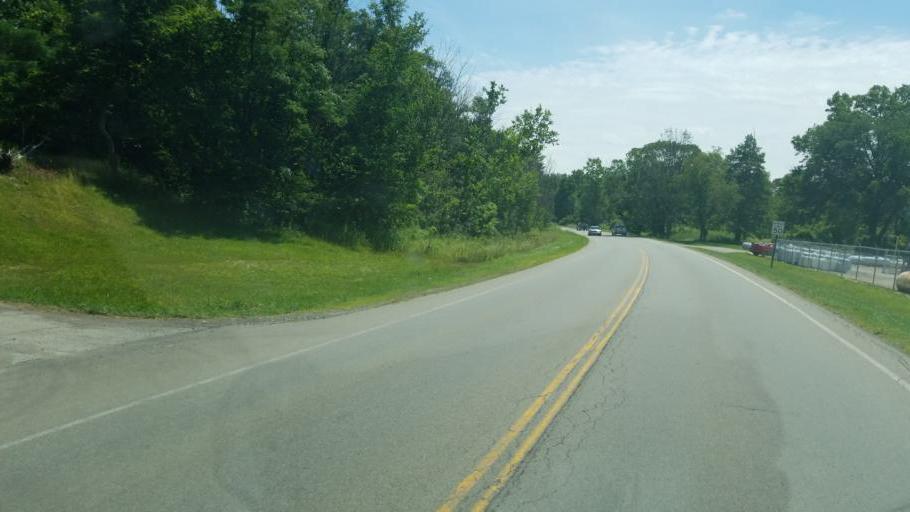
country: US
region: Ohio
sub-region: Richland County
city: Lincoln Heights
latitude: 40.8332
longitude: -82.5131
